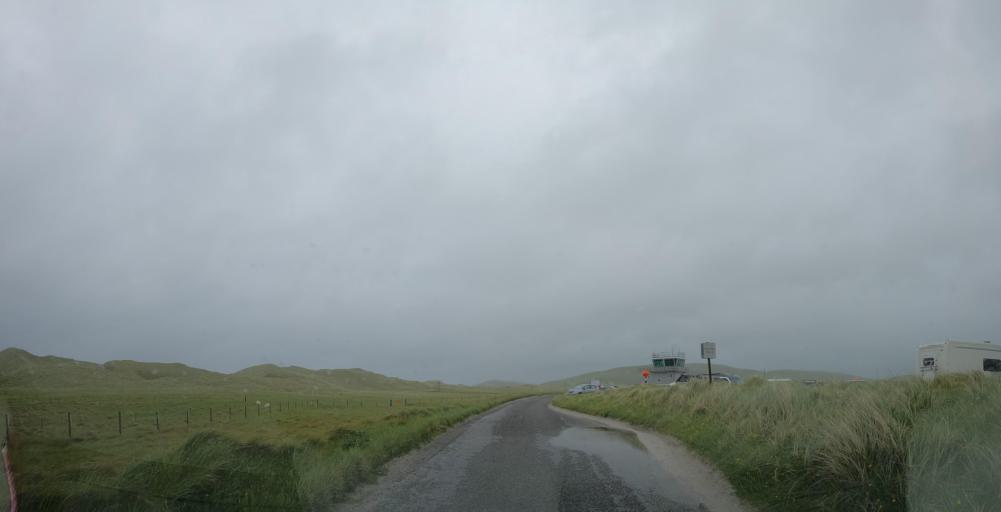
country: GB
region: Scotland
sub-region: Eilean Siar
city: Barra
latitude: 57.0246
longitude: -7.4501
